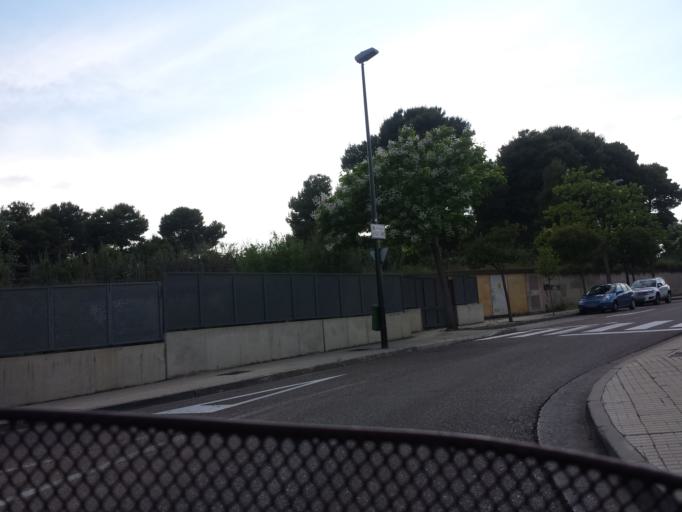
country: ES
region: Aragon
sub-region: Provincia de Zaragoza
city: Montecanal
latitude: 41.6303
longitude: -0.9174
